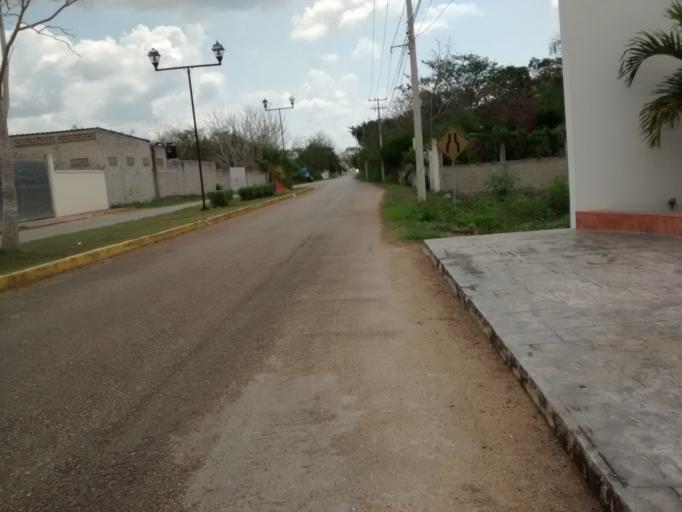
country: MX
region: Yucatan
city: Valladolid
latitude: 20.6866
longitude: -88.2200
